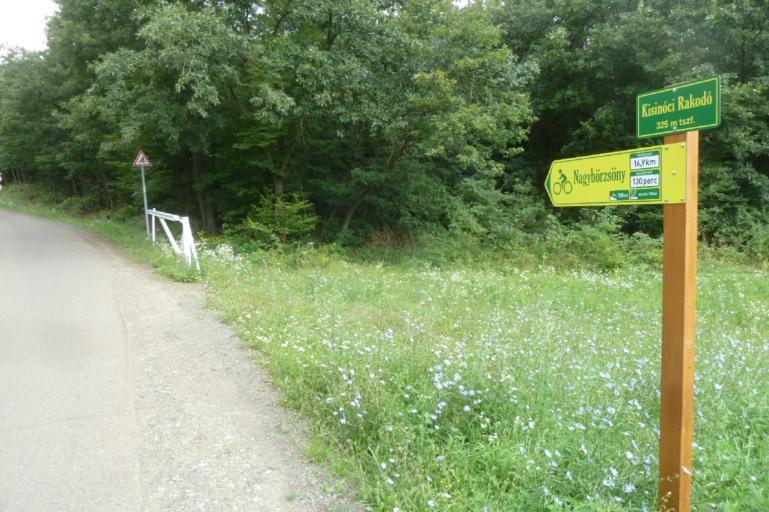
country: HU
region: Pest
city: Szob
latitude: 47.8914
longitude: 18.9270
